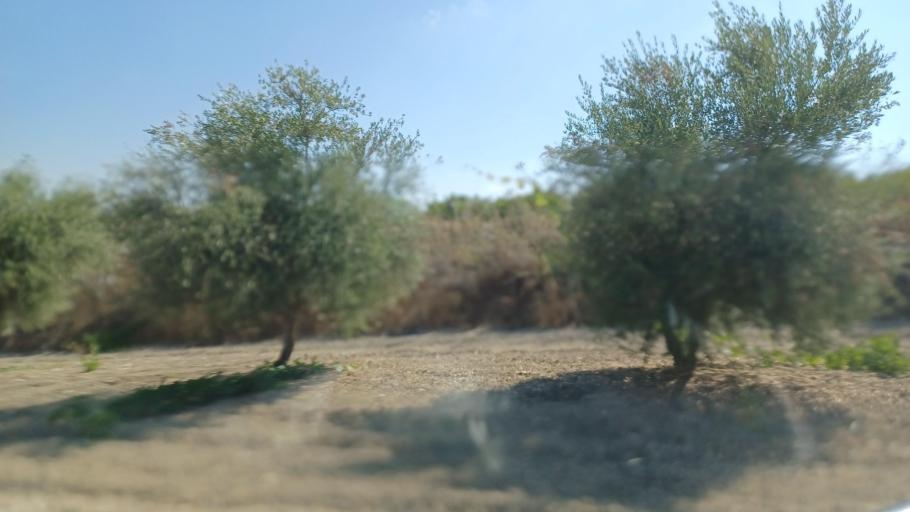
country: CY
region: Pafos
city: Tala
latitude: 34.9026
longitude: 32.4886
